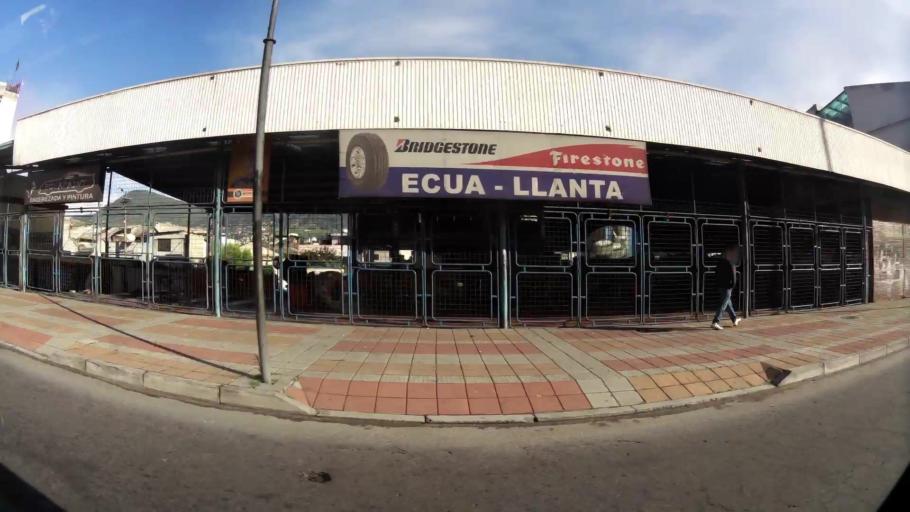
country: EC
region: Pichincha
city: Quito
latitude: -0.2393
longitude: -78.5106
